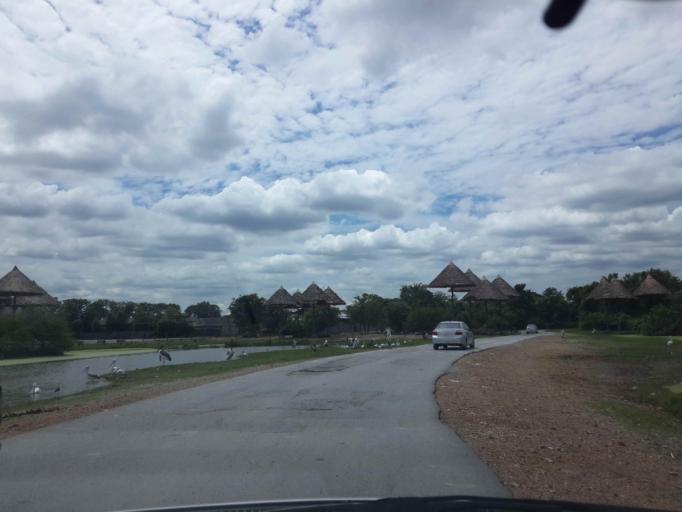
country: TH
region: Bangkok
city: Khlong Sam Wa
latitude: 13.8645
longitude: 100.7052
